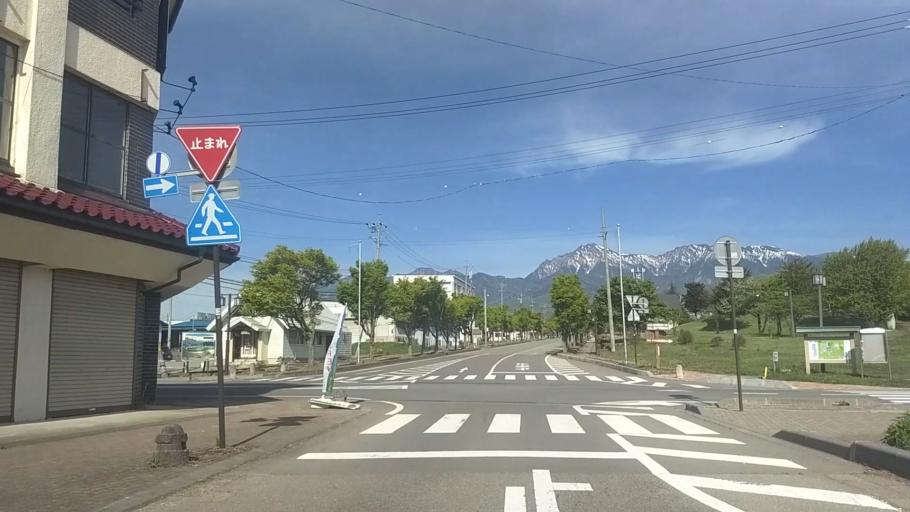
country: JP
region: Yamanashi
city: Nirasaki
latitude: 35.9555
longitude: 138.4741
